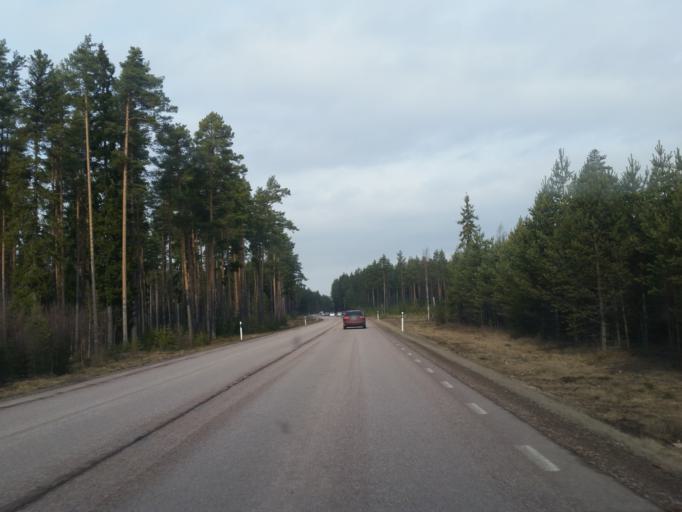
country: SE
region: Dalarna
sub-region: Mora Kommun
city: Mora
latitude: 60.9777
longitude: 14.6935
